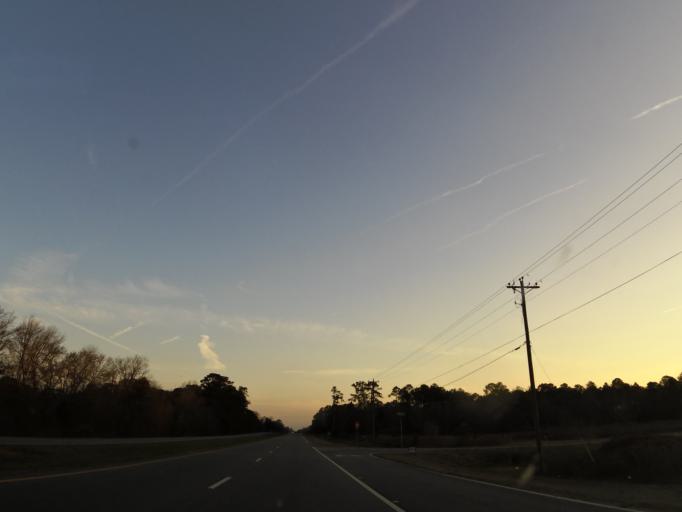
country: US
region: Georgia
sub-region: Lee County
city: Leesburg
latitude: 31.7078
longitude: -84.1726
